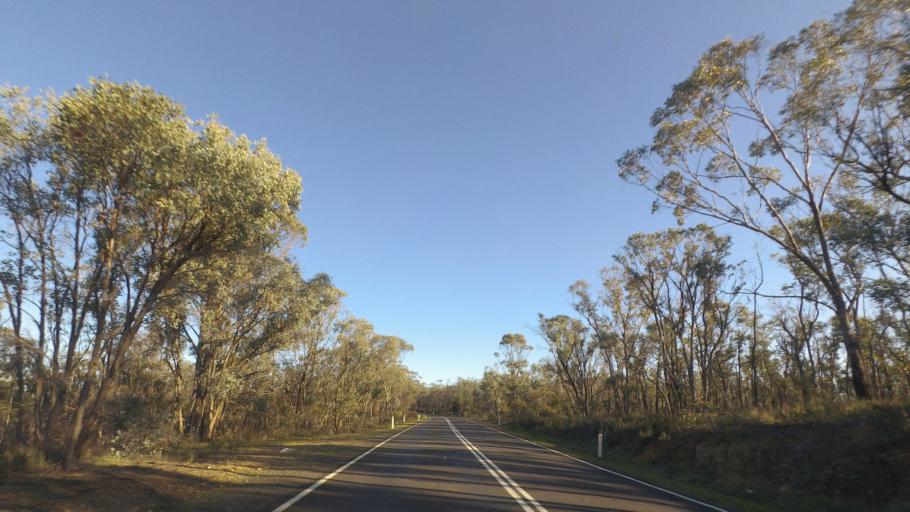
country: AU
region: Victoria
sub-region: Greater Bendigo
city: Kennington
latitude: -36.9229
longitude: 144.4905
